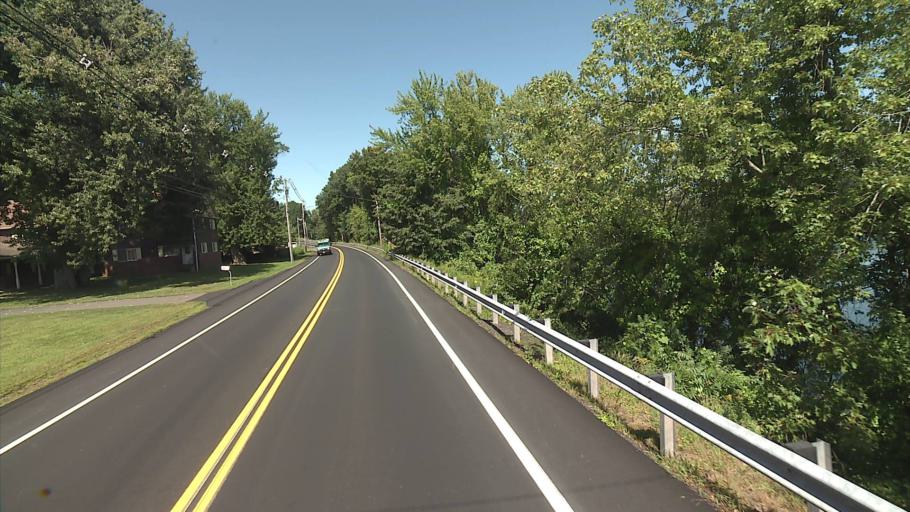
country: US
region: Connecticut
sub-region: Hartford County
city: Windsor Locks
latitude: 41.9066
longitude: -72.6249
